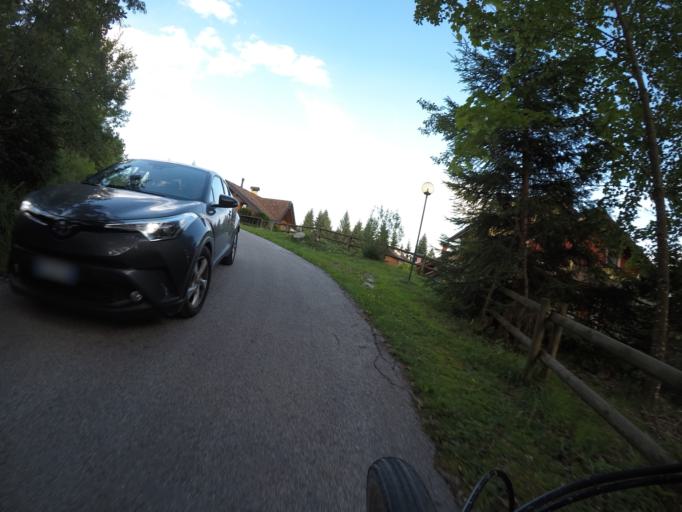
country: IT
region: Veneto
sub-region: Provincia di Vicenza
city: Gallio
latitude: 45.8879
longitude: 11.5310
